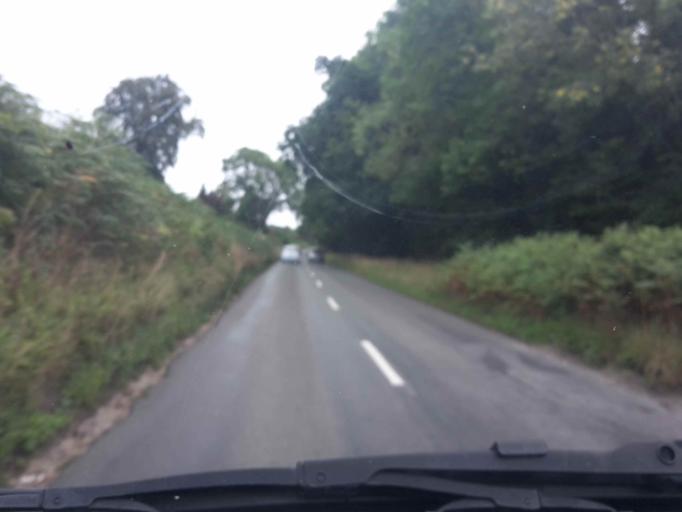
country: GB
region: England
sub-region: Oxfordshire
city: Rotherfield Peppard
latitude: 51.5439
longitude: -0.9534
